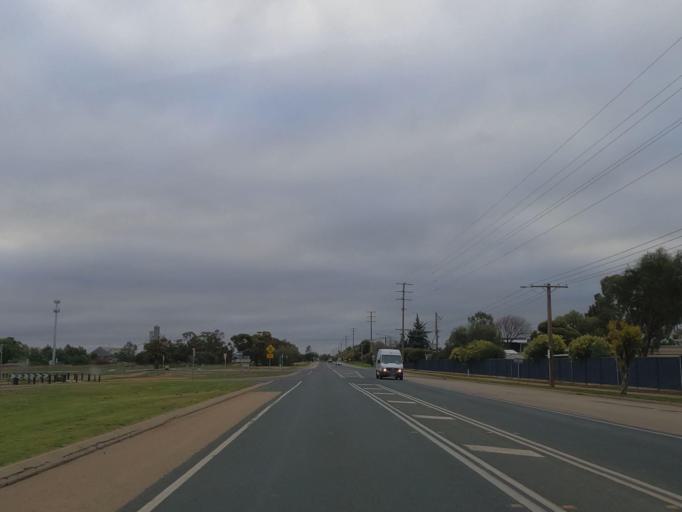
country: AU
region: Victoria
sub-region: Swan Hill
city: Swan Hill
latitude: -35.4626
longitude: 143.6351
